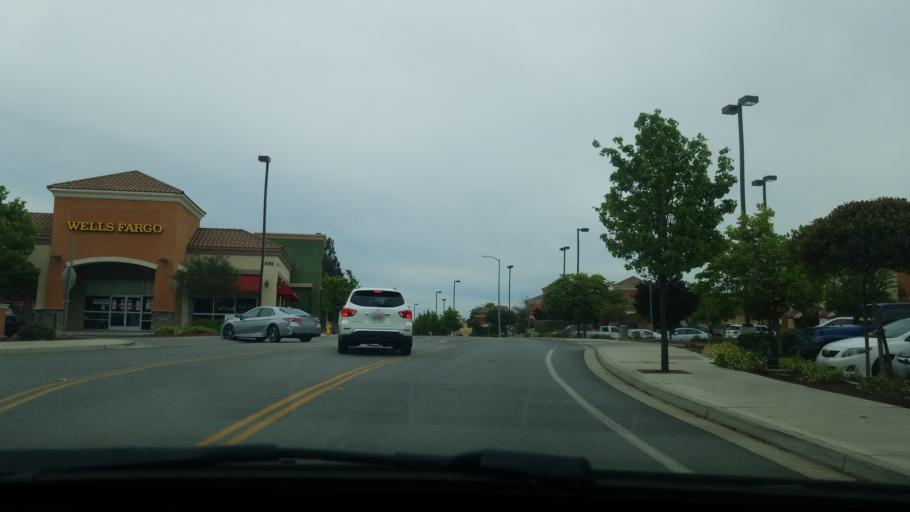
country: US
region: California
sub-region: San Luis Obispo County
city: Nipomo
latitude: 35.0353
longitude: -120.4864
